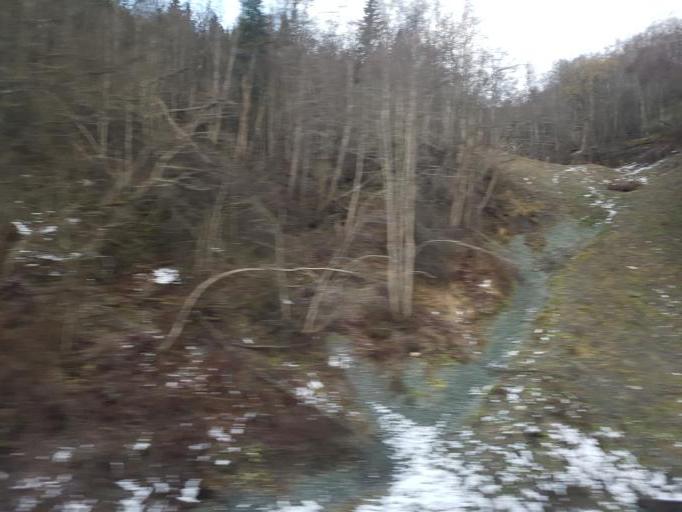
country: NO
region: Sor-Trondelag
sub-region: Midtre Gauldal
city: Storen
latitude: 62.9776
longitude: 10.2280
